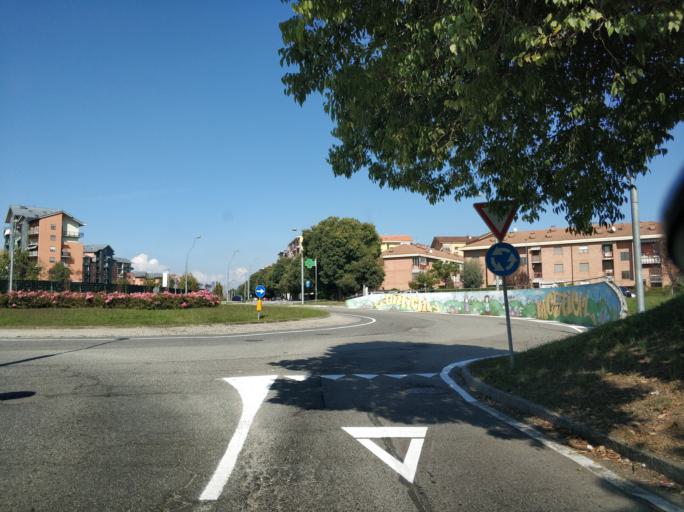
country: IT
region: Piedmont
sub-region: Provincia di Torino
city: Settimo Torinese
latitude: 45.1443
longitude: 7.7758
